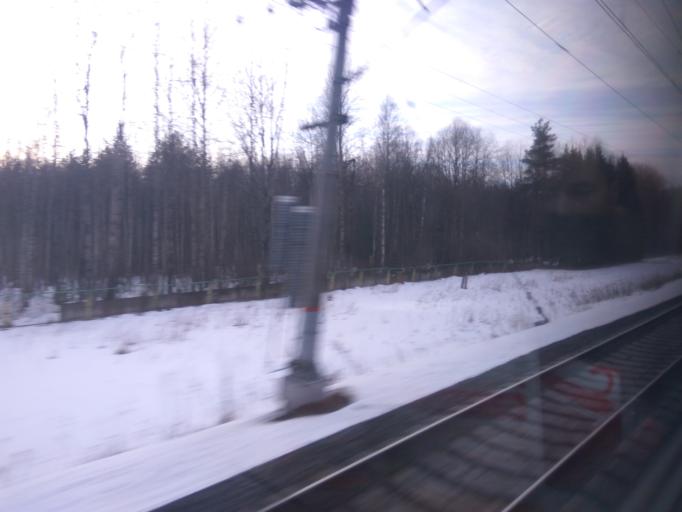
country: RU
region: Novgorod
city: Chudovo
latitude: 59.0969
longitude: 31.7269
